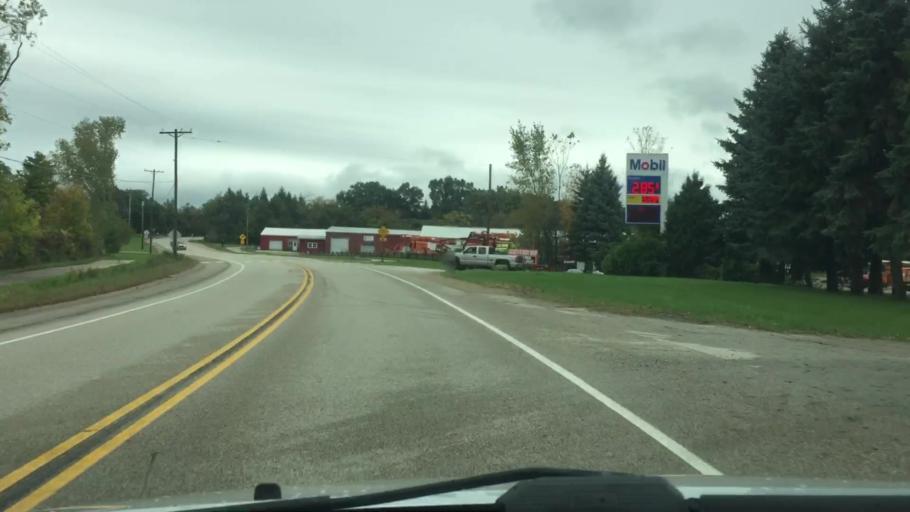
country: US
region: Wisconsin
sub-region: Waukesha County
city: Dousman
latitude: 43.0164
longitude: -88.4625
